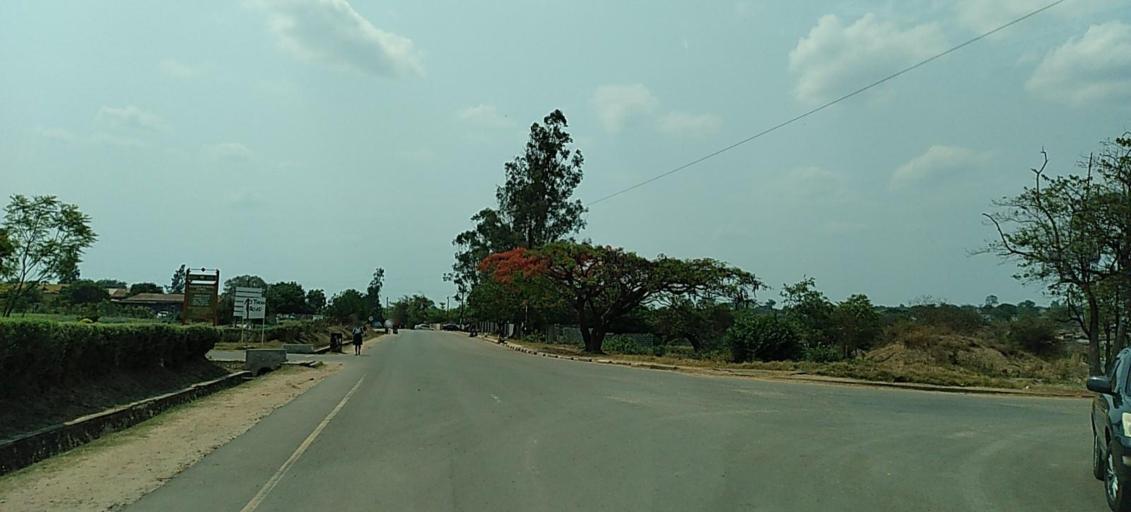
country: ZM
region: Copperbelt
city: Chambishi
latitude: -12.6401
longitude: 28.0609
